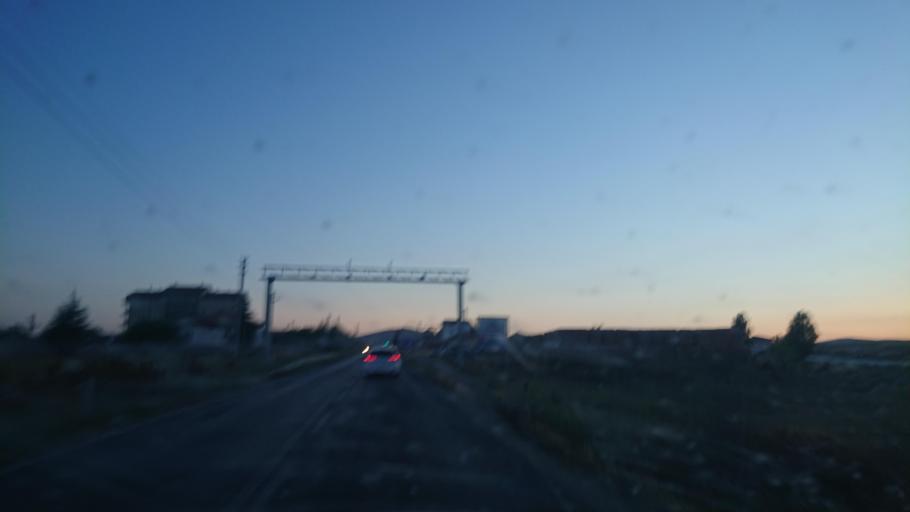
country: TR
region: Aksaray
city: Balci
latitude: 38.7565
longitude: 34.0761
